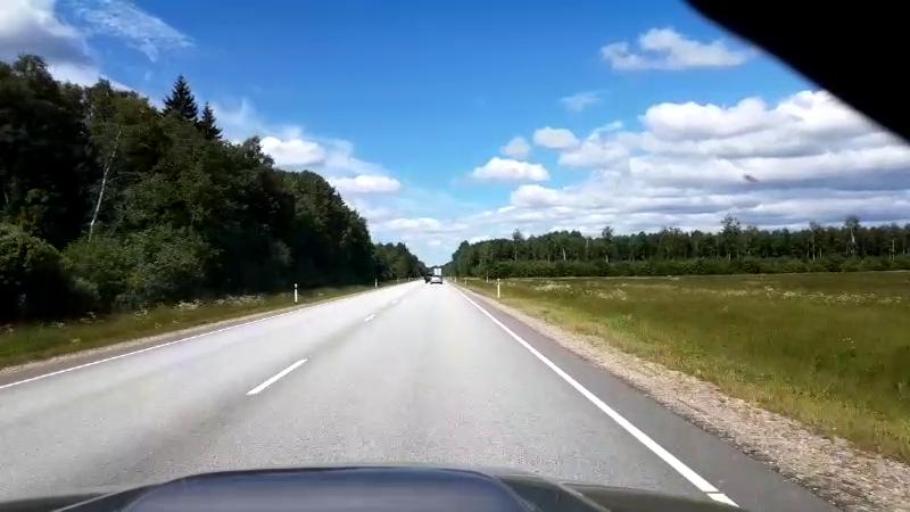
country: EE
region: Paernumaa
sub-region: Halinga vald
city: Parnu-Jaagupi
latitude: 58.5407
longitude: 24.5440
